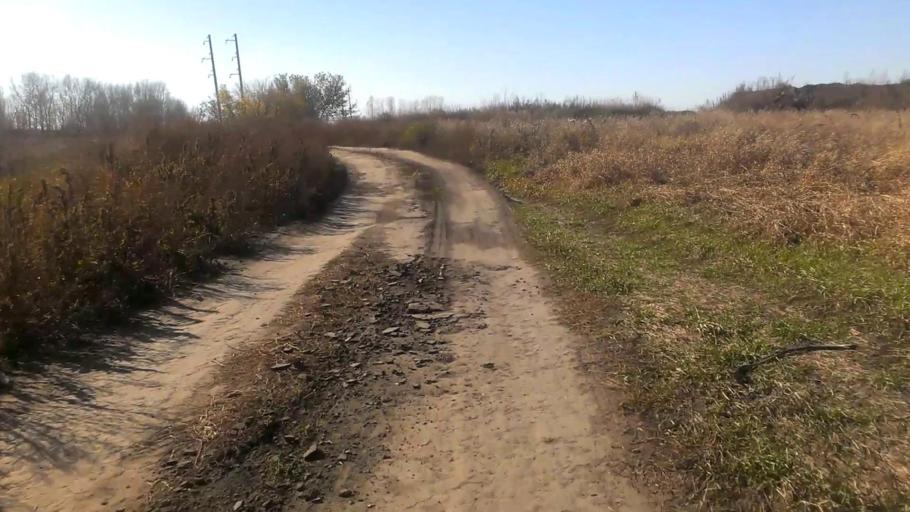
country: RU
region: Altai Krai
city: Novoaltaysk
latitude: 53.3698
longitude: 83.9503
